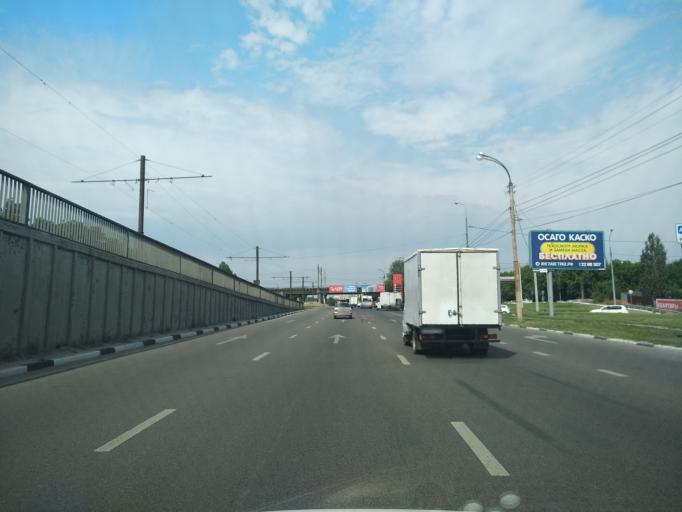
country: RU
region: Voronezj
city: Voronezh
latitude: 51.6941
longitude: 39.2317
